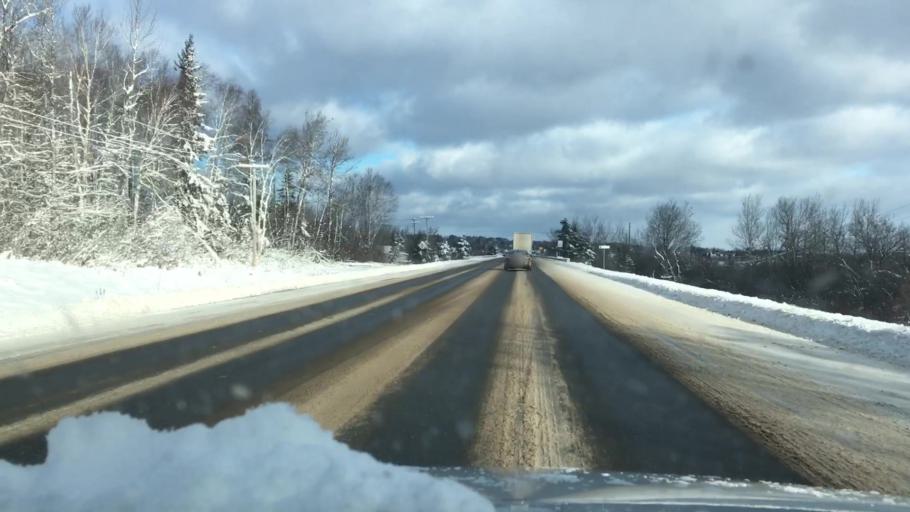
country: US
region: Maine
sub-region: Aroostook County
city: Caribou
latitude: 46.8458
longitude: -68.0039
